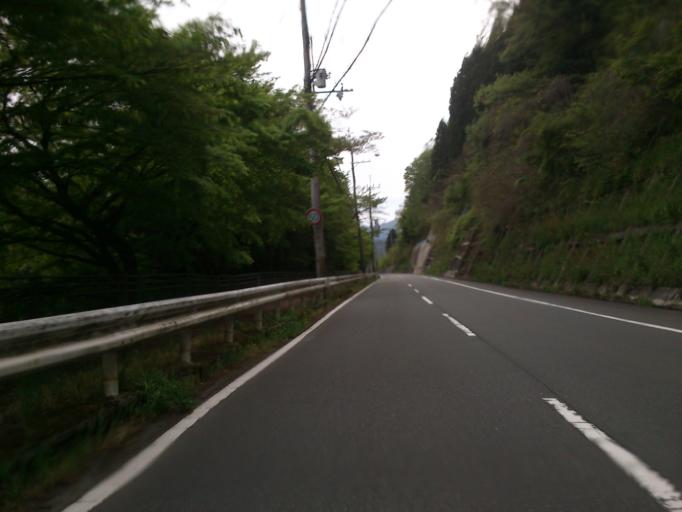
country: JP
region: Kyoto
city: Maizuru
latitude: 35.2703
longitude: 135.4953
